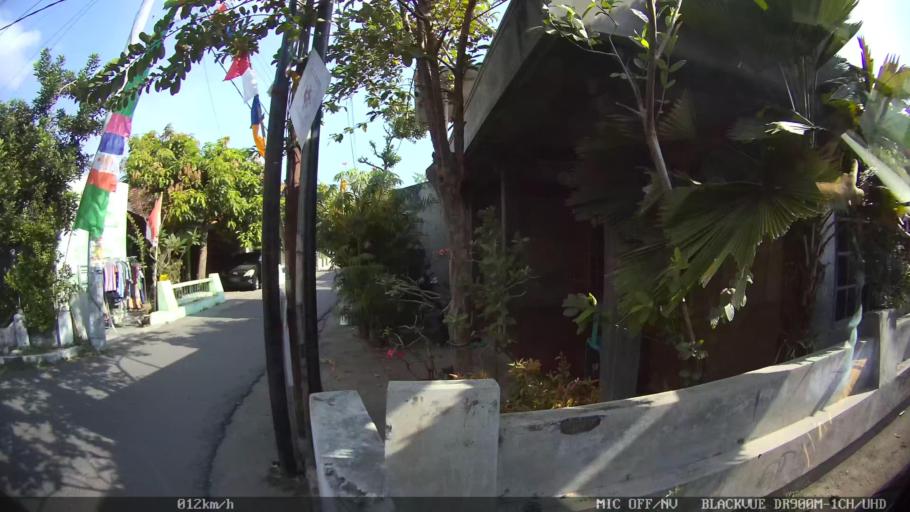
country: ID
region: Daerah Istimewa Yogyakarta
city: Sewon
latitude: -7.8343
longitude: 110.3965
